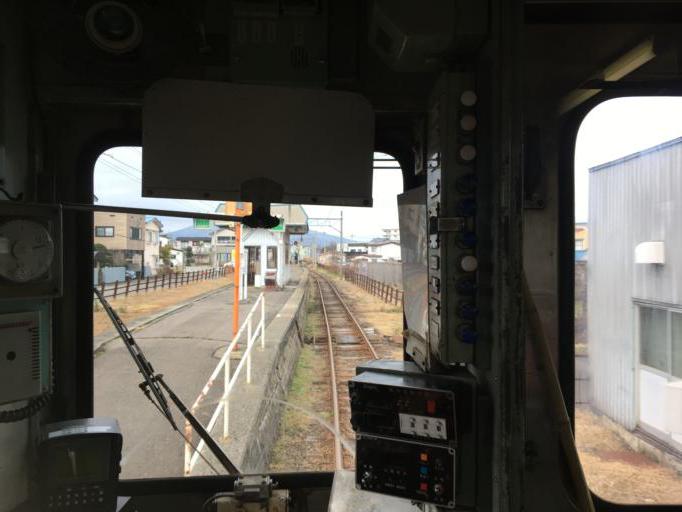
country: JP
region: Aomori
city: Hirosaki
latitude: 40.5671
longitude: 140.4807
